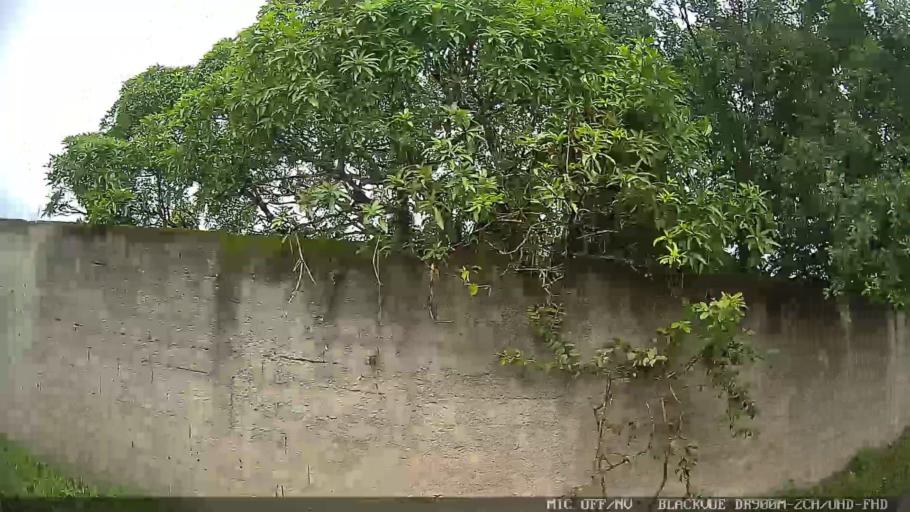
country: BR
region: Sao Paulo
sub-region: Sao Sebastiao
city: Sao Sebastiao
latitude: -23.7097
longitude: -45.4559
